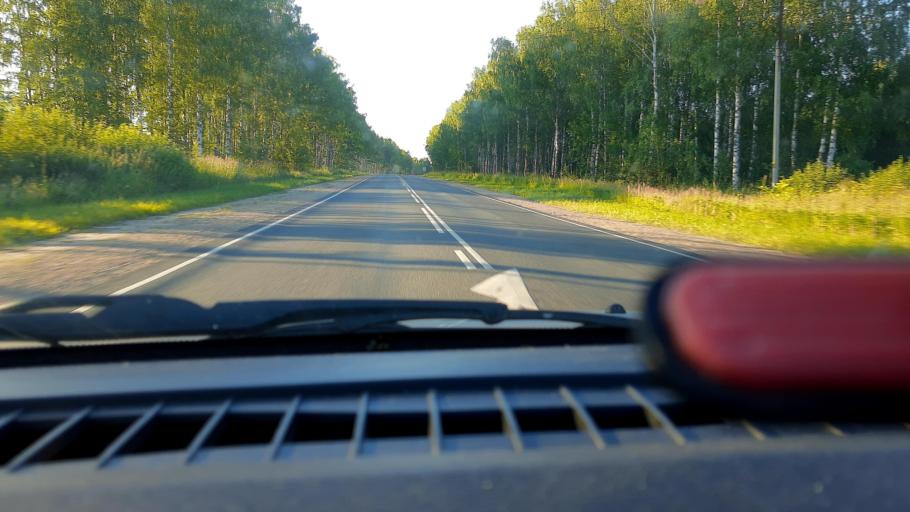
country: RU
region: Nizjnij Novgorod
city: Krasnyye Baki
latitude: 57.0548
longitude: 45.1364
